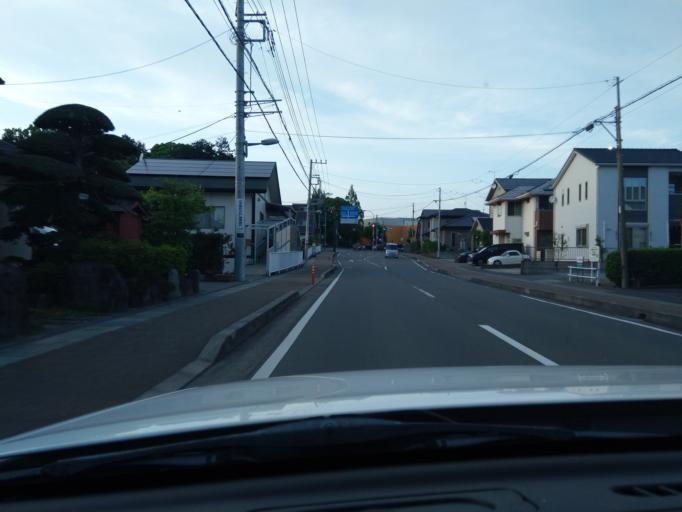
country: JP
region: Shizuoka
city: Mishima
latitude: 35.1464
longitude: 138.8906
